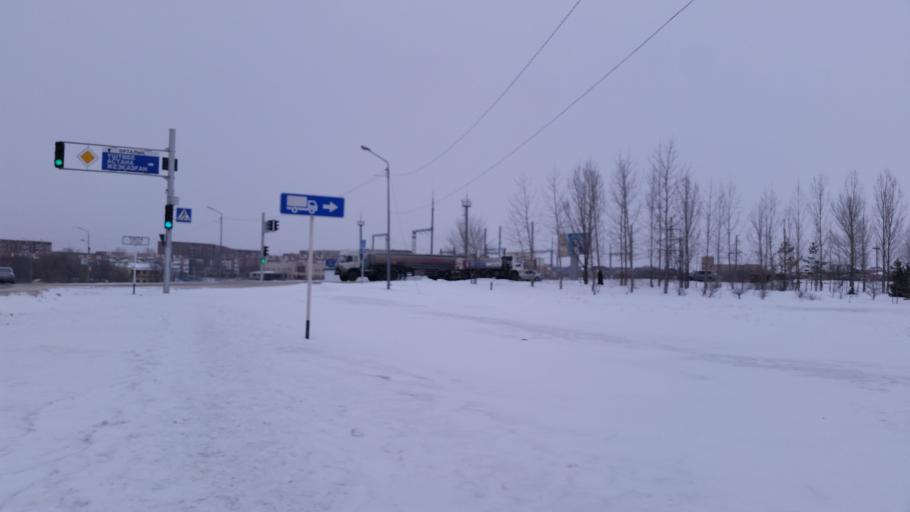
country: KZ
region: Qaraghandy
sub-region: Qaraghandy Qalasy
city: Karagandy
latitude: 49.7748
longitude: 73.1562
